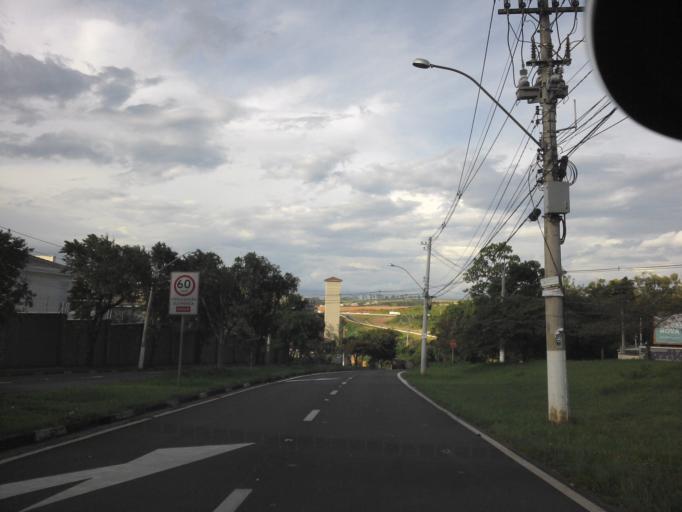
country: BR
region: Sao Paulo
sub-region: Campinas
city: Campinas
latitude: -22.8698
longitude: -47.0255
